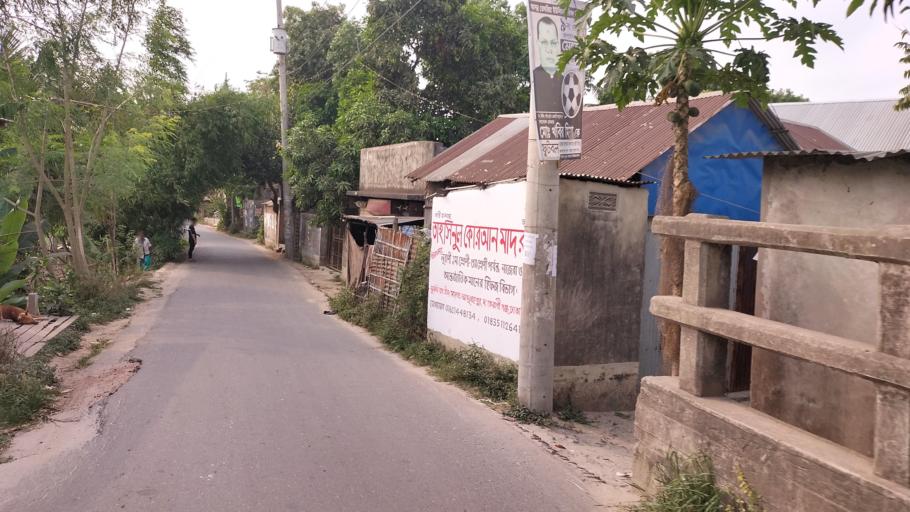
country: BD
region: Dhaka
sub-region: Dhaka
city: Dhaka
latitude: 23.6636
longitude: 90.3540
